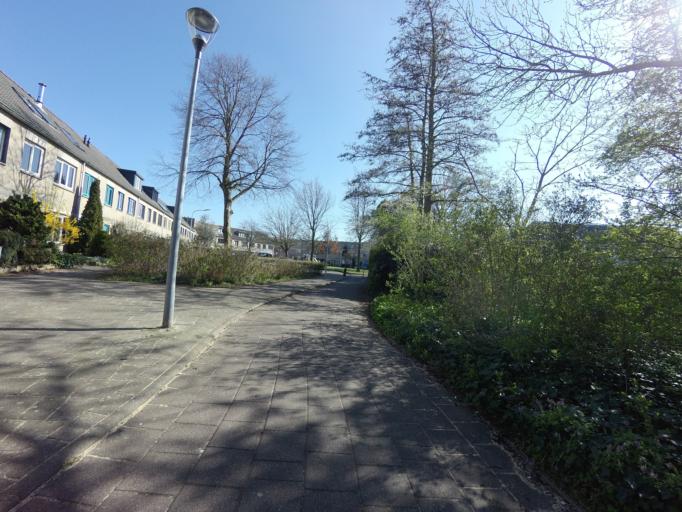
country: NL
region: North Holland
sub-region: Gemeente Haarlem
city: Haarlem
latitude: 52.3750
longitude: 4.6222
